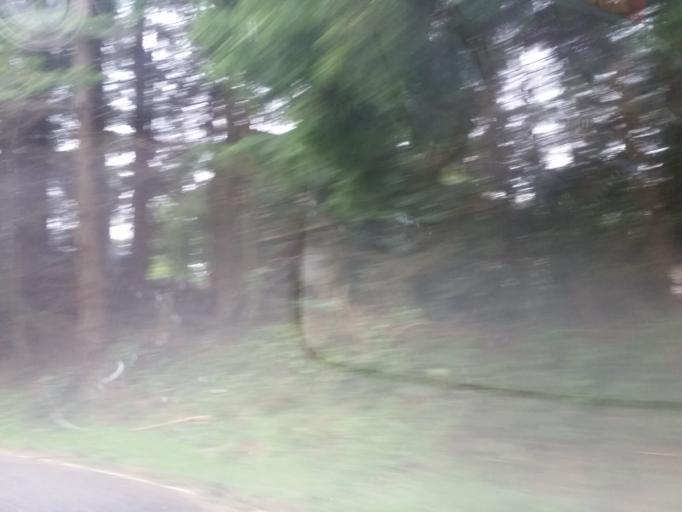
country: US
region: Washington
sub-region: Snohomish County
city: Meadowdale
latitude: 47.8358
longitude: -122.3413
